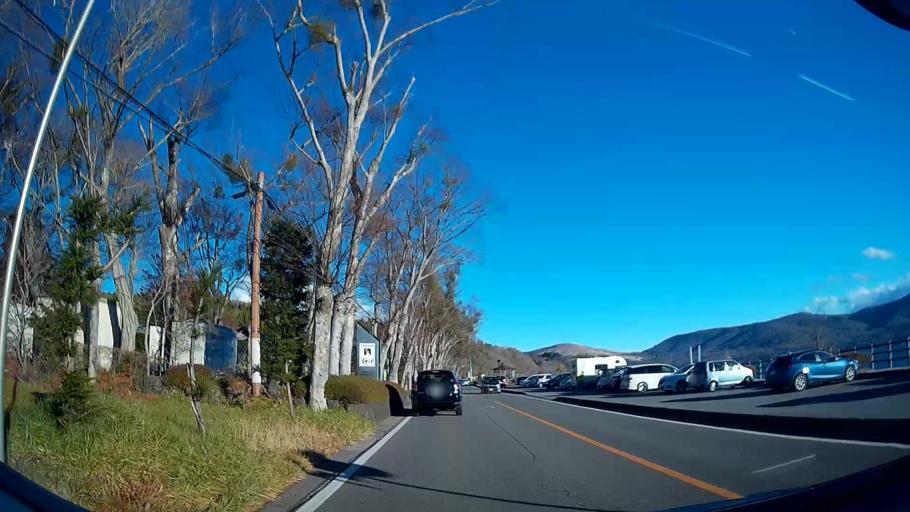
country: JP
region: Shizuoka
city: Gotemba
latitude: 35.4274
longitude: 138.8700
